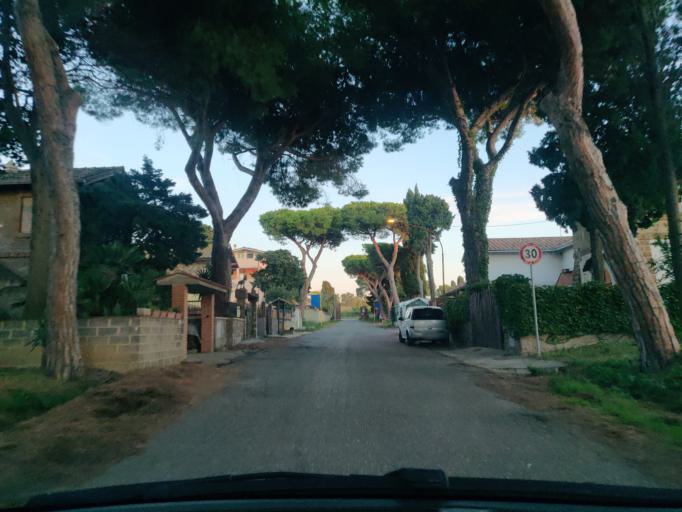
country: IT
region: Latium
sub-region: Citta metropolitana di Roma Capitale
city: Aurelia
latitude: 42.1374
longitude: 11.7868
